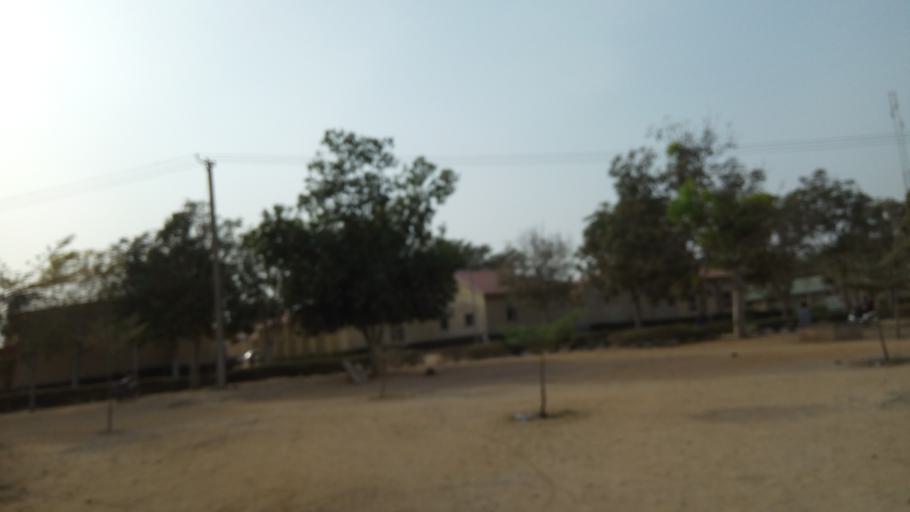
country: NG
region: Gombe
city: Gombe
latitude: 10.3053
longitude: 11.1751
